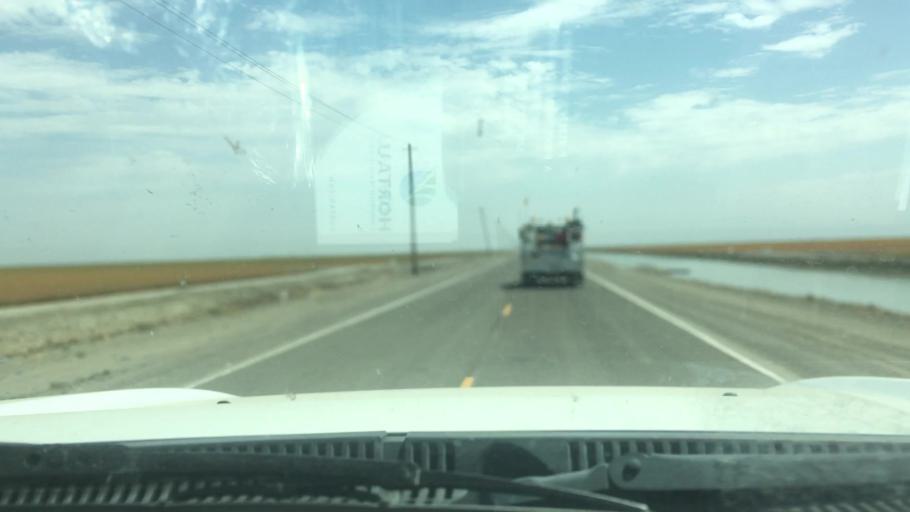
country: US
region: California
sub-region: Tulare County
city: Alpaugh
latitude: 35.9217
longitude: -119.5733
